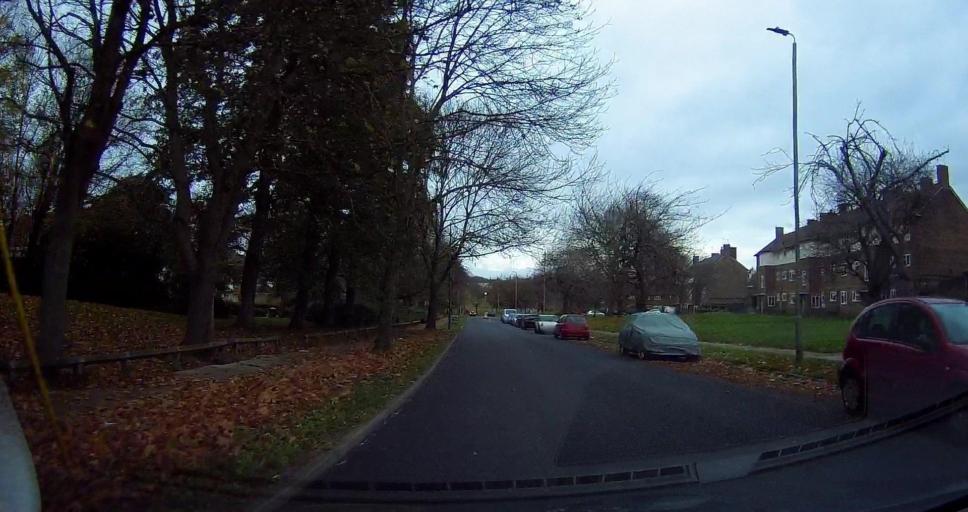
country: GB
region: England
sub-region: Greater London
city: Sidcup
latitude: 51.4064
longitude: 0.1044
